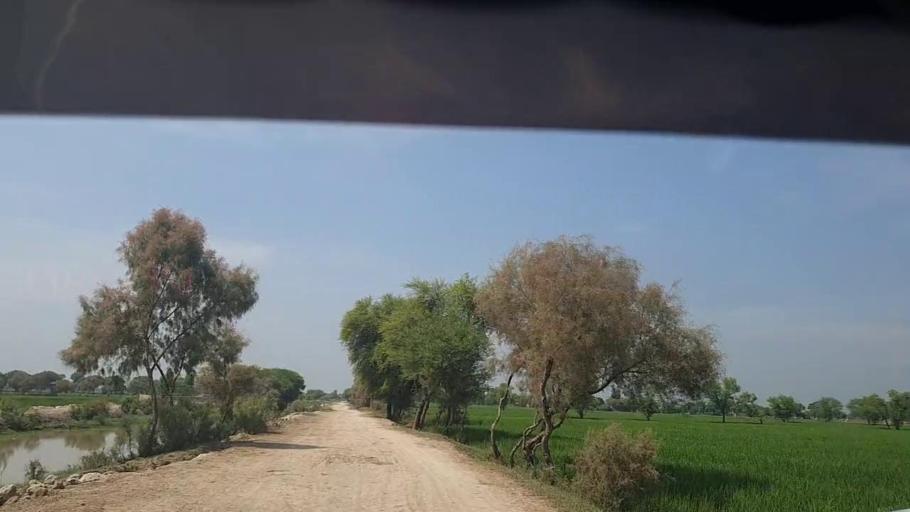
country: PK
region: Sindh
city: Thul
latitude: 28.1971
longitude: 68.7052
